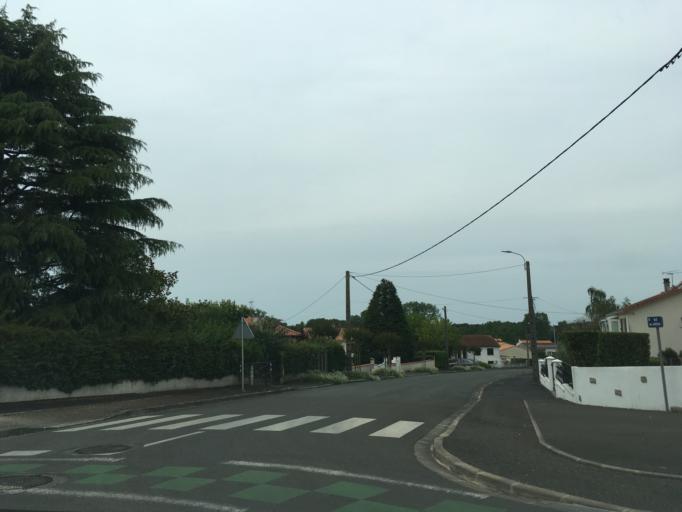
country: FR
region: Poitou-Charentes
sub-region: Departement des Deux-Sevres
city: Bessines
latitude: 46.3186
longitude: -0.5159
